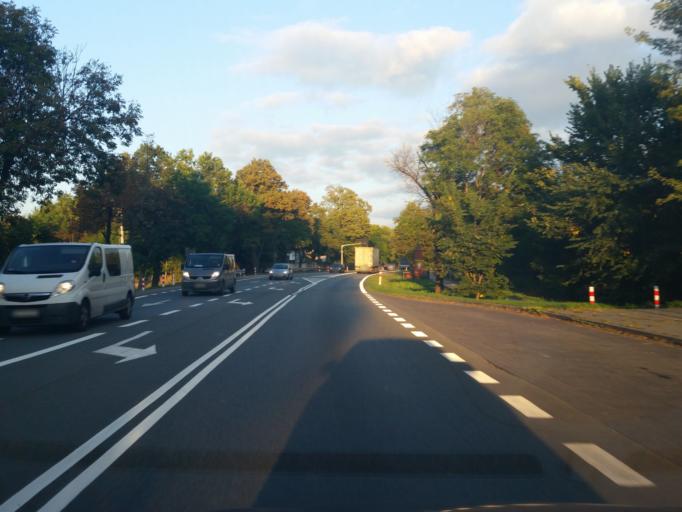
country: PL
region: Masovian Voivodeship
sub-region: Powiat warszawski zachodni
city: Jozefow
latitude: 52.2126
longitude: 20.6954
